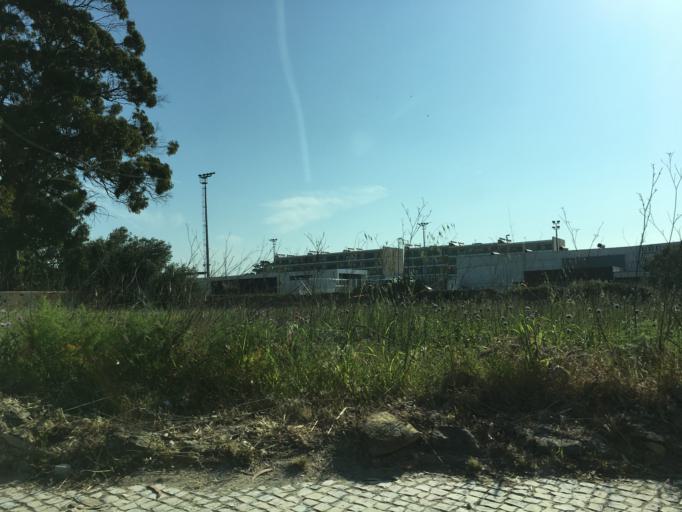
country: PT
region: Lisbon
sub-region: Cascais
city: Parede
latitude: 38.7211
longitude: -9.3494
